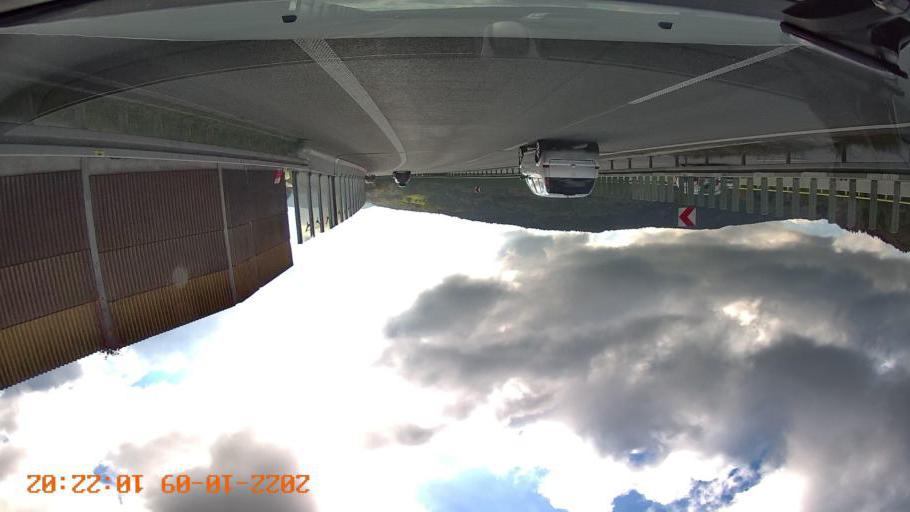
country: PL
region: Lesser Poland Voivodeship
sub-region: Powiat myslenicki
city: Stroza
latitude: 49.7854
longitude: 19.9503
